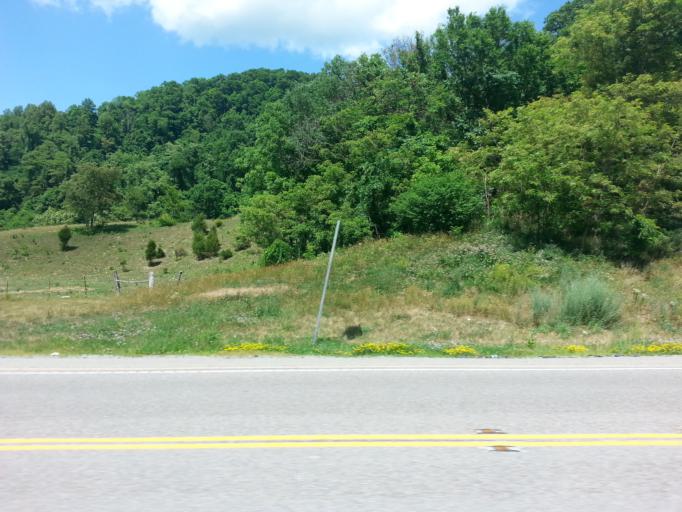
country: US
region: Virginia
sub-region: Lee County
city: Dryden
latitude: 36.7170
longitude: -82.9292
